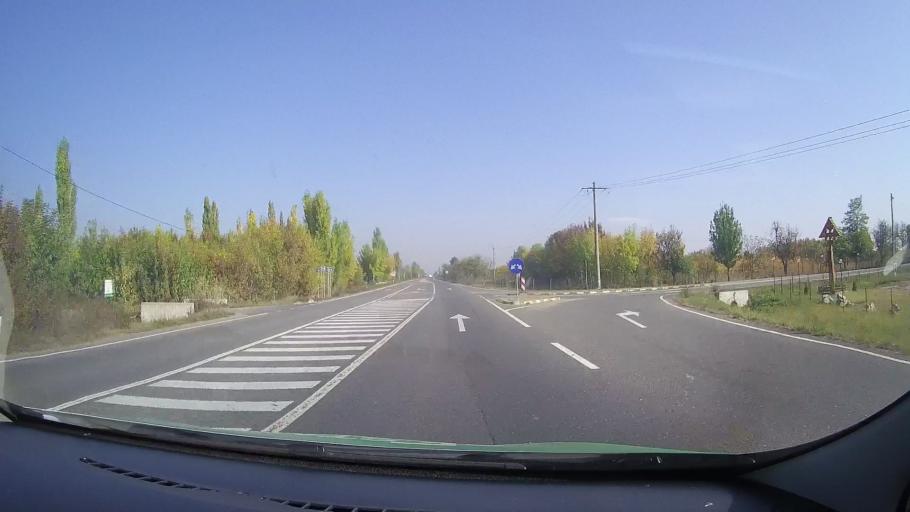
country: RO
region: Bihor
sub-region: Comuna Madaras
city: Madaras
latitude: 46.8486
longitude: 21.7148
